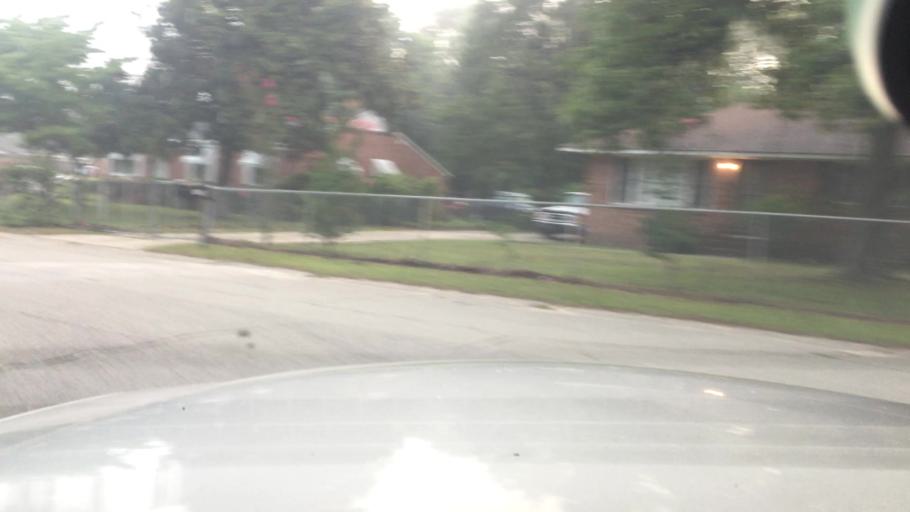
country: US
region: North Carolina
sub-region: Cumberland County
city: Hope Mills
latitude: 35.0229
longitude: -78.9422
